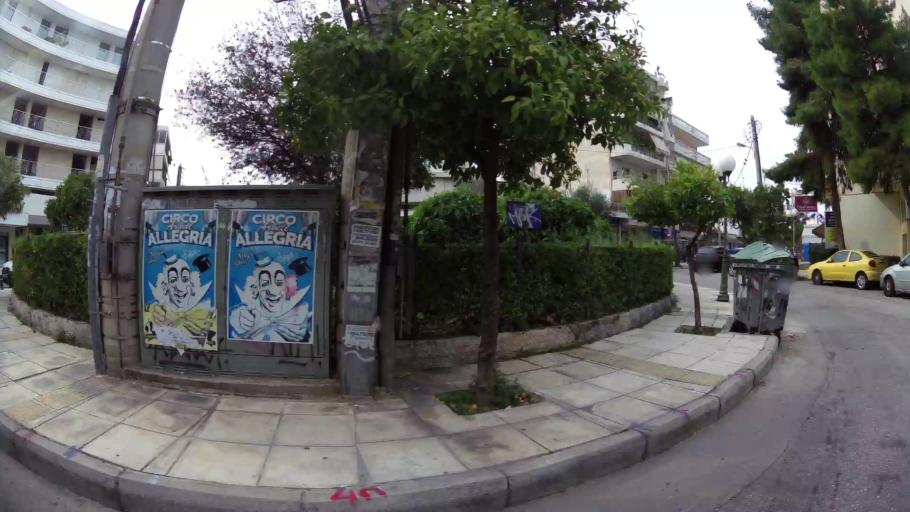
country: GR
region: Attica
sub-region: Nomarchia Athinas
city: Nea Ionia
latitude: 38.0341
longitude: 23.7595
